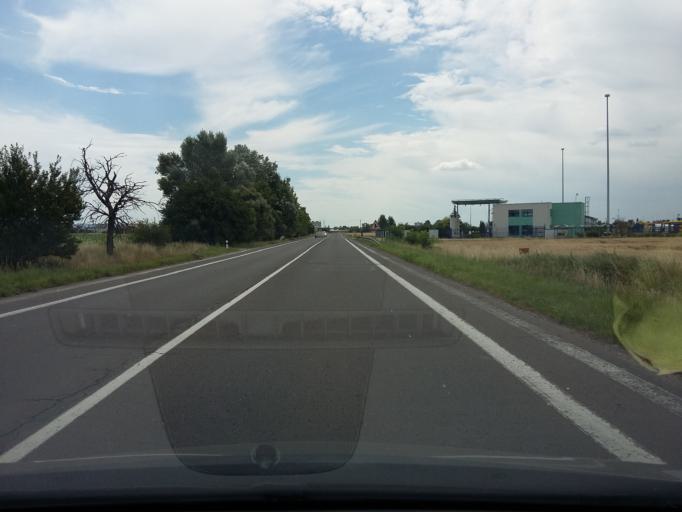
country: SK
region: Bratislavsky
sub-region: Okres Malacky
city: Malacky
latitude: 48.4537
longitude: 17.0106
